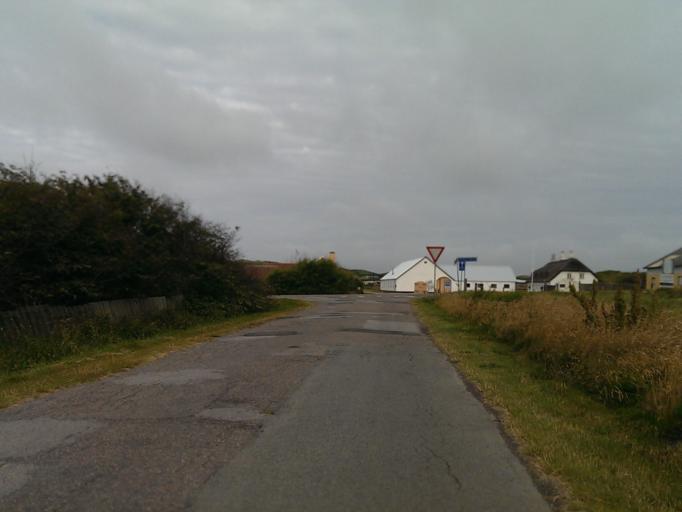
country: DK
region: North Denmark
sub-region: Jammerbugt Kommune
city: Pandrup
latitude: 57.3810
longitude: 9.7264
